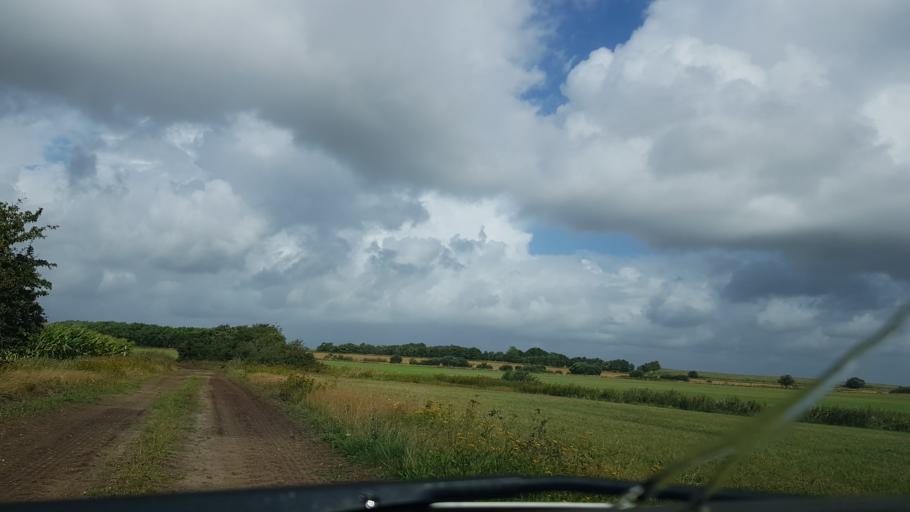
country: DK
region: South Denmark
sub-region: Esbjerg Kommune
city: Ribe
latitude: 55.2533
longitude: 8.7653
